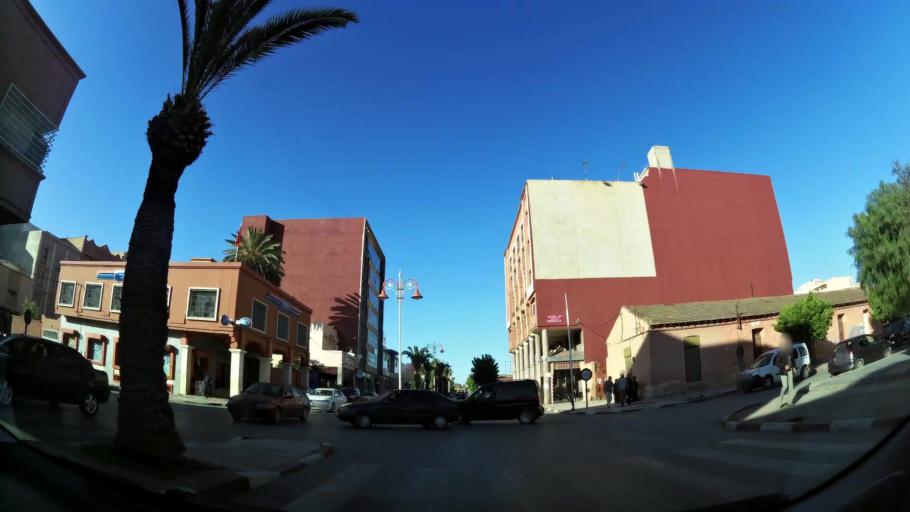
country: MA
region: Oriental
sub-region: Berkane-Taourirt
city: Berkane
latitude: 34.9256
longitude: -2.3332
